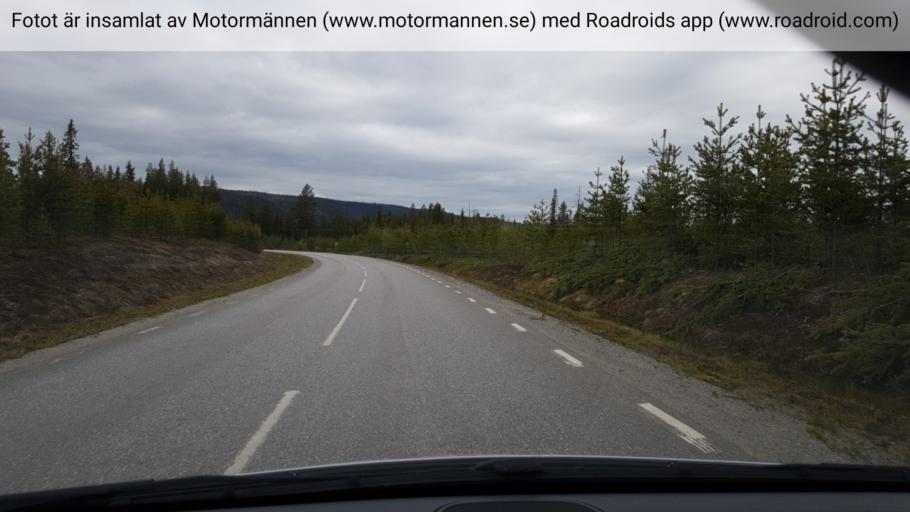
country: SE
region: Vaesterbotten
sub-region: Sorsele Kommun
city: Sorsele
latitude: 65.5455
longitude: 17.4254
